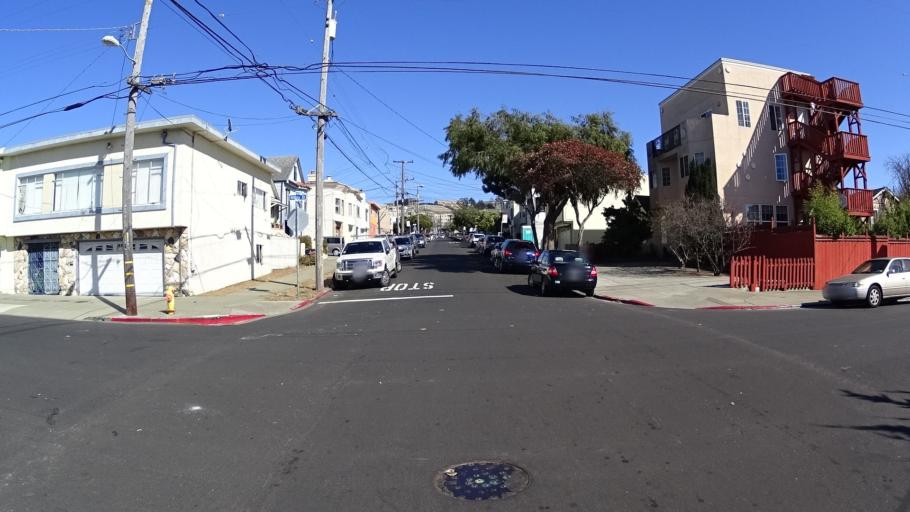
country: US
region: California
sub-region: San Mateo County
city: Daly City
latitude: 37.7031
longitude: -122.4687
